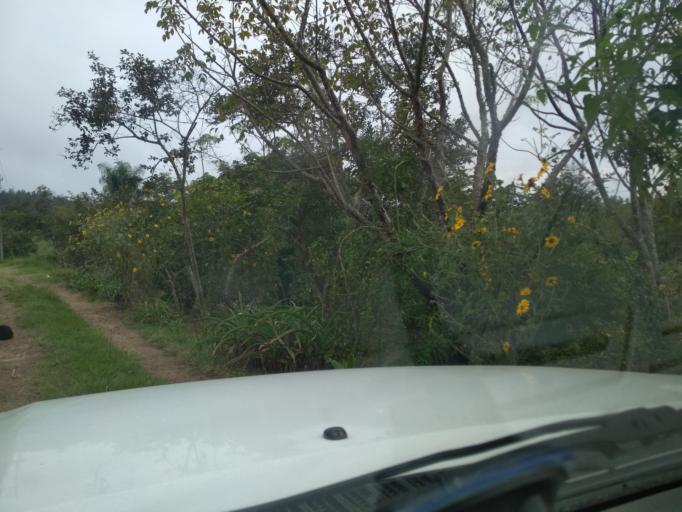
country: MX
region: Veracruz
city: El Castillo
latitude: 19.5408
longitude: -96.8337
